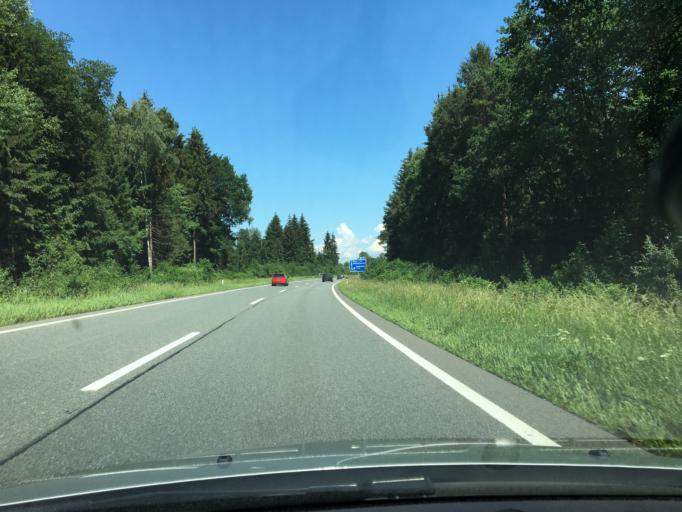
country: DE
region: Bavaria
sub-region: Upper Bavaria
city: Ainring
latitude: 47.7733
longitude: 12.9811
